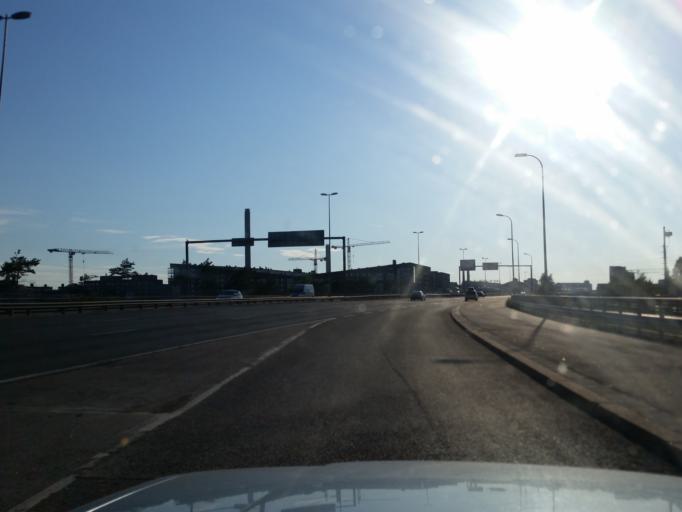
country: FI
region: Uusimaa
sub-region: Helsinki
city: Helsinki
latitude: 60.1859
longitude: 24.9914
